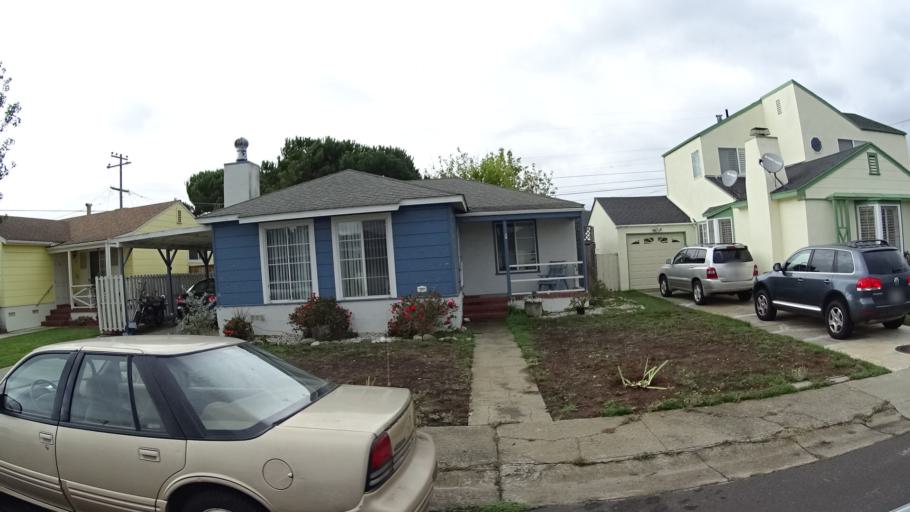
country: US
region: California
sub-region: San Mateo County
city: San Bruno
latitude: 37.6382
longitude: -122.4291
